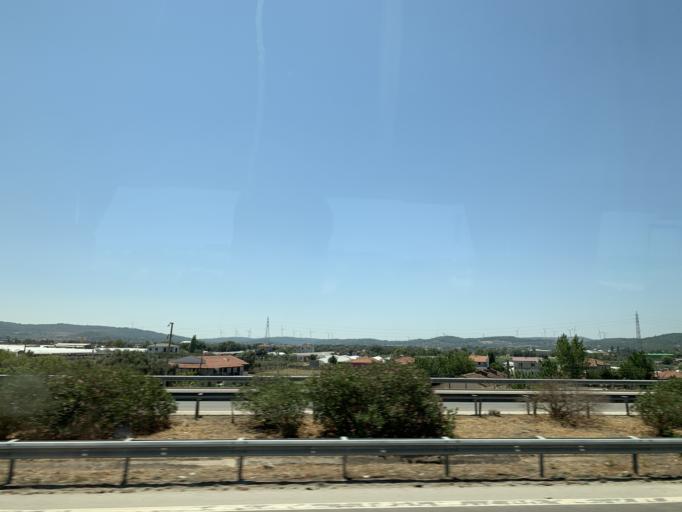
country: TR
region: Izmir
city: Urla
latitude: 38.2975
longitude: 26.7348
